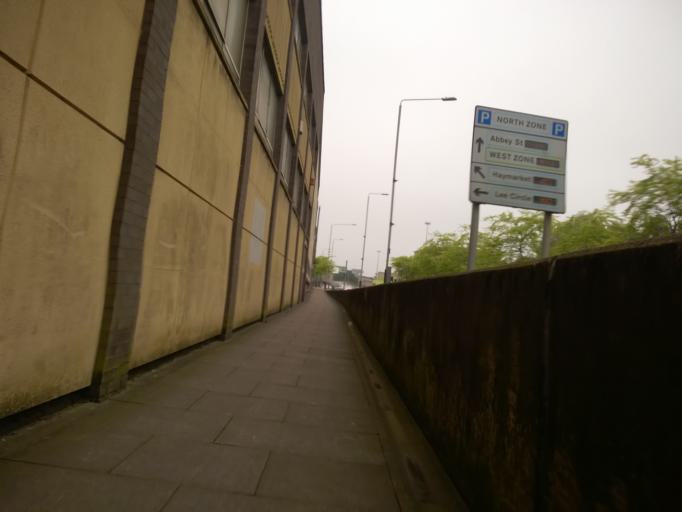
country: GB
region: England
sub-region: City of Leicester
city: Leicester
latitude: 52.6394
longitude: -1.1259
